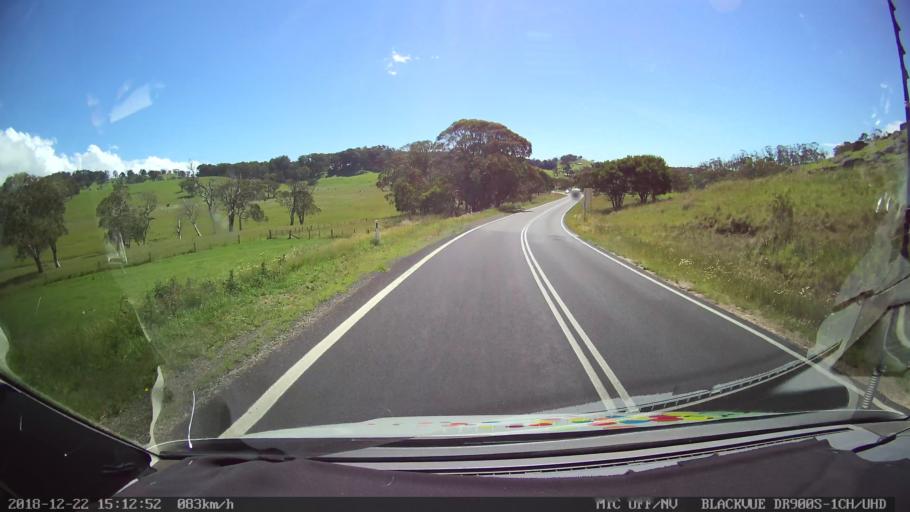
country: AU
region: New South Wales
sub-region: Bellingen
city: Dorrigo
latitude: -30.3601
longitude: 152.3962
